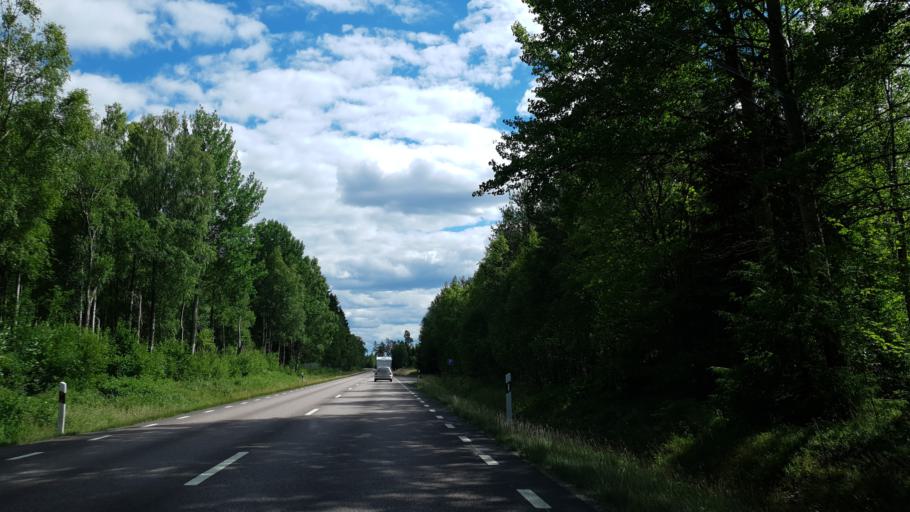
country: SE
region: Kronoberg
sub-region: Lessebo Kommun
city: Lessebo
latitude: 56.8395
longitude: 15.3913
